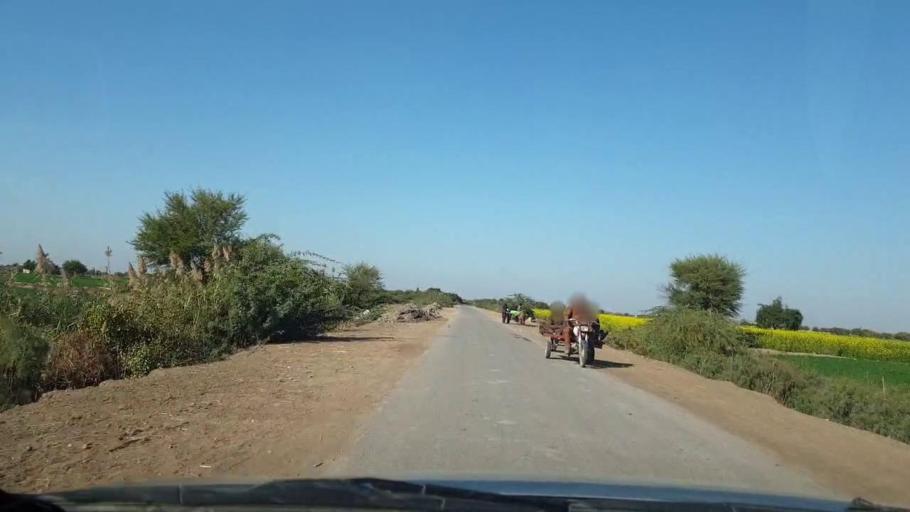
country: PK
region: Sindh
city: Jhol
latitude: 25.8237
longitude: 68.9481
